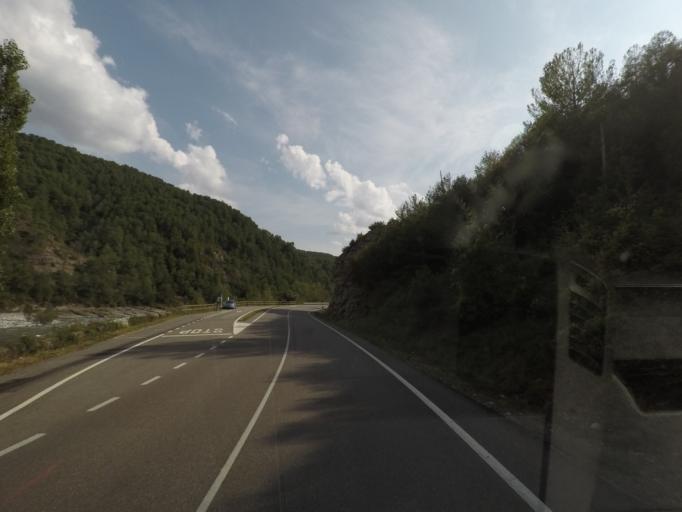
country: ES
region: Aragon
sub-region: Provincia de Huesca
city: Puertolas
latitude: 42.5449
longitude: 0.1593
